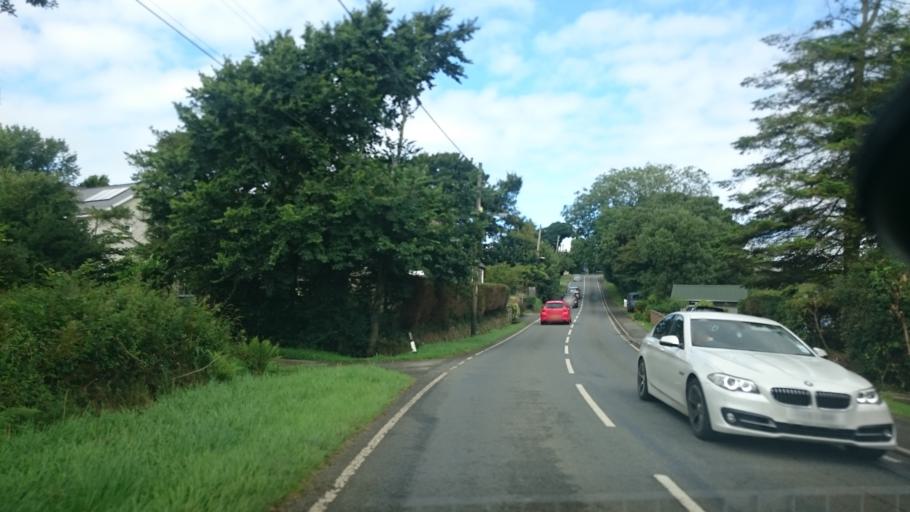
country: GB
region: Wales
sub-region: Pembrokeshire
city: Freystrop
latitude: 51.7615
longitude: -4.9600
